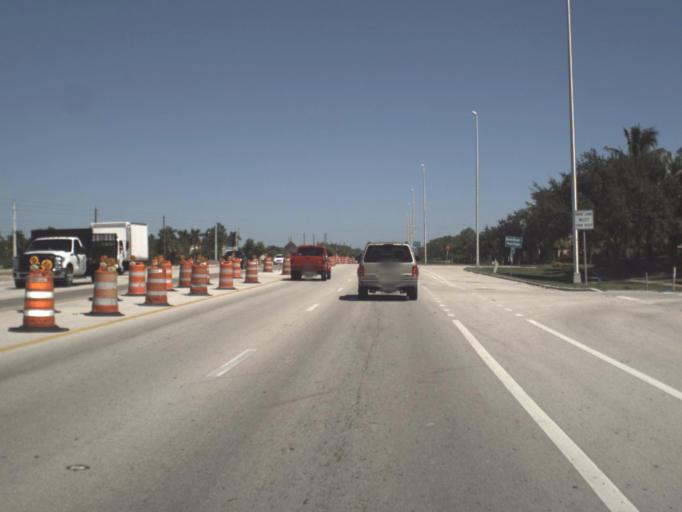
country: US
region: Florida
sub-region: Collier County
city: Lely Resort
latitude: 26.0641
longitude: -81.6986
